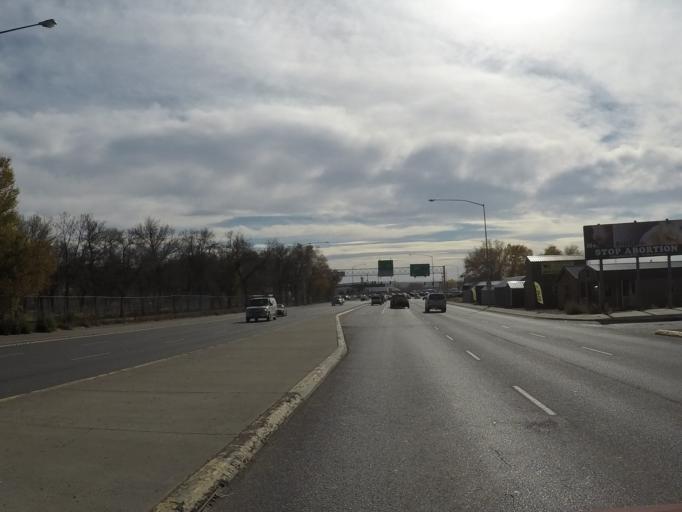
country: US
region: Montana
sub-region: Yellowstone County
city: Billings
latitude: 45.7964
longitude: -108.4814
